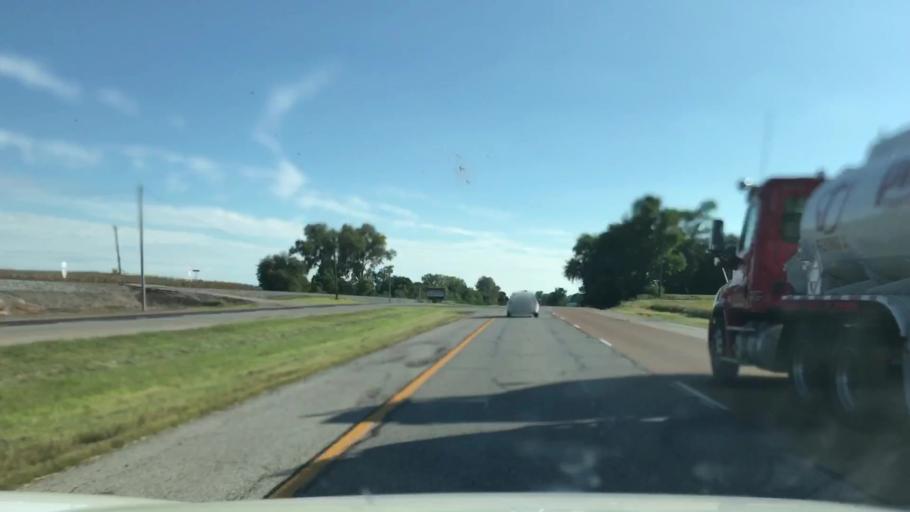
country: US
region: Illinois
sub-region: Madison County
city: Mitchell
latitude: 38.7886
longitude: -90.1057
